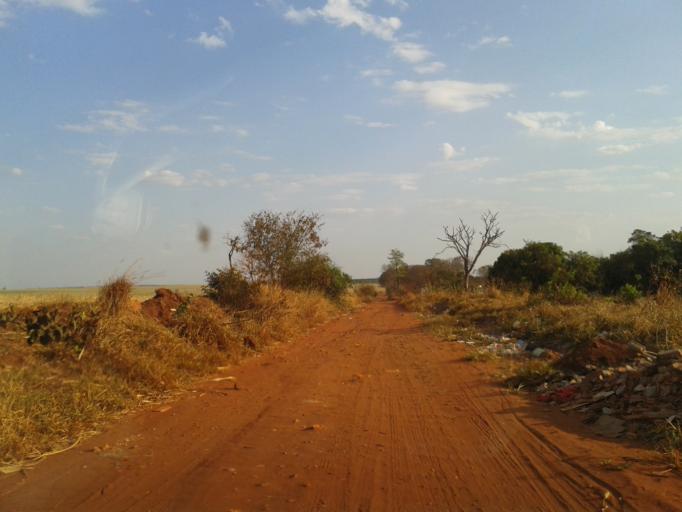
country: BR
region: Minas Gerais
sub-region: Ituiutaba
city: Ituiutaba
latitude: -18.9983
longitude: -49.4349
